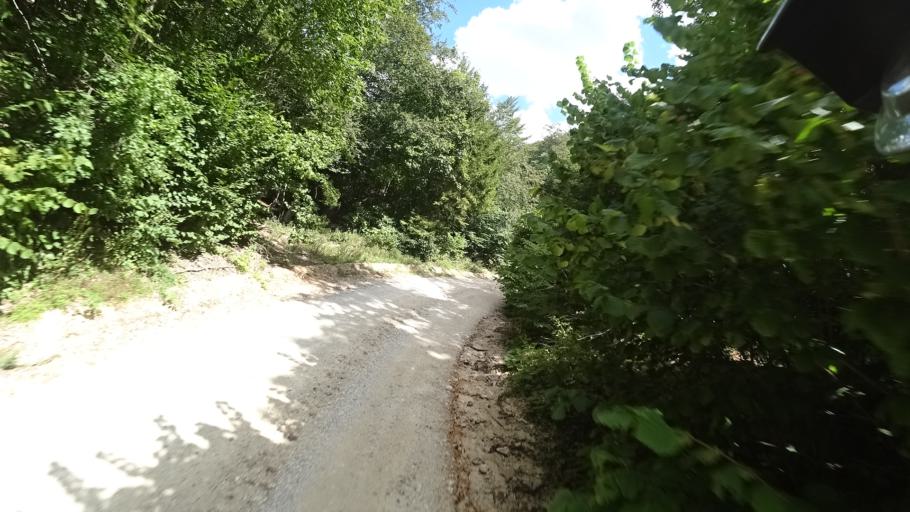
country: BA
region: Federation of Bosnia and Herzegovina
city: Orasac
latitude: 44.5707
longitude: 15.8489
